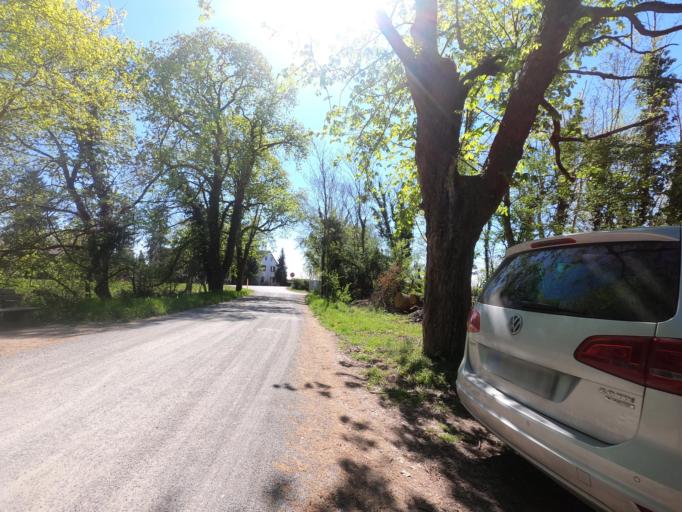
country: DE
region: Hesse
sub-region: Regierungsbezirk Darmstadt
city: Gross-Gerau
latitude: 49.9426
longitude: 8.4995
